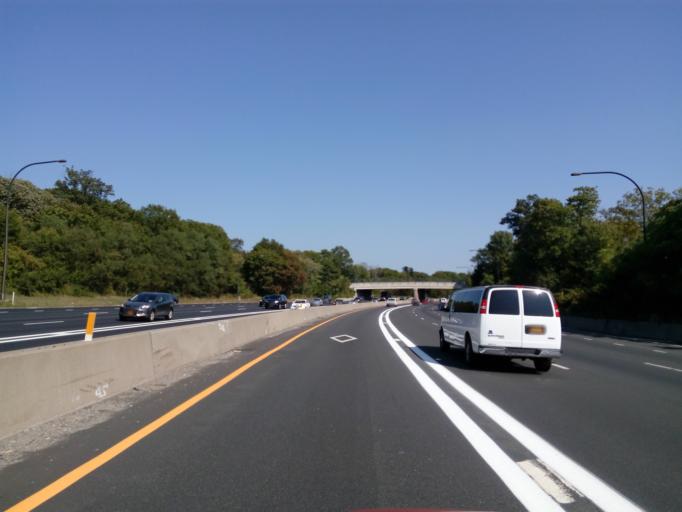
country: US
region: New York
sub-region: Nassau County
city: East Hills
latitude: 40.7836
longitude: -73.6176
